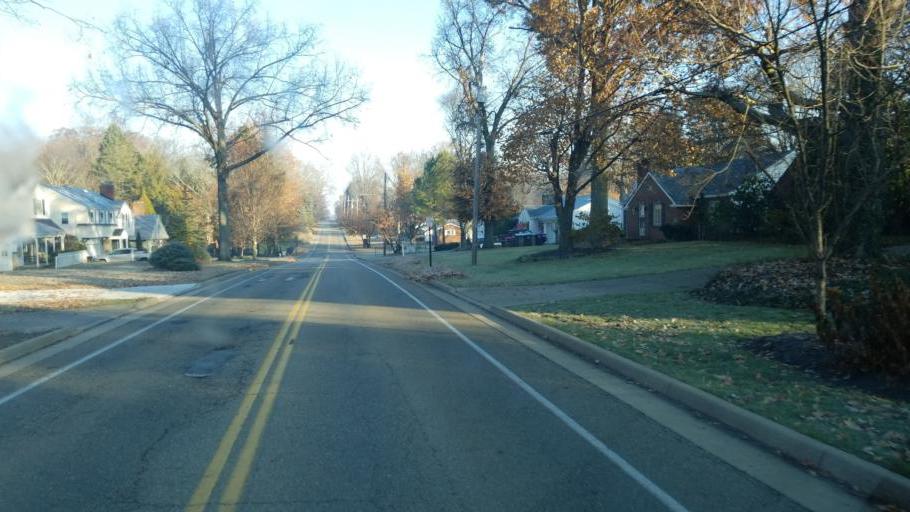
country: US
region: Ohio
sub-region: Summit County
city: Fairlawn
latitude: 41.1222
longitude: -81.5876
